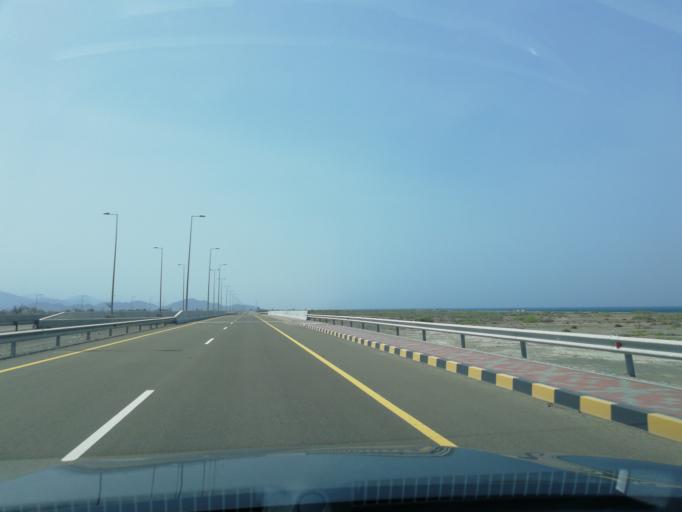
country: OM
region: Al Batinah
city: Shinas
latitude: 24.8960
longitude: 56.3988
